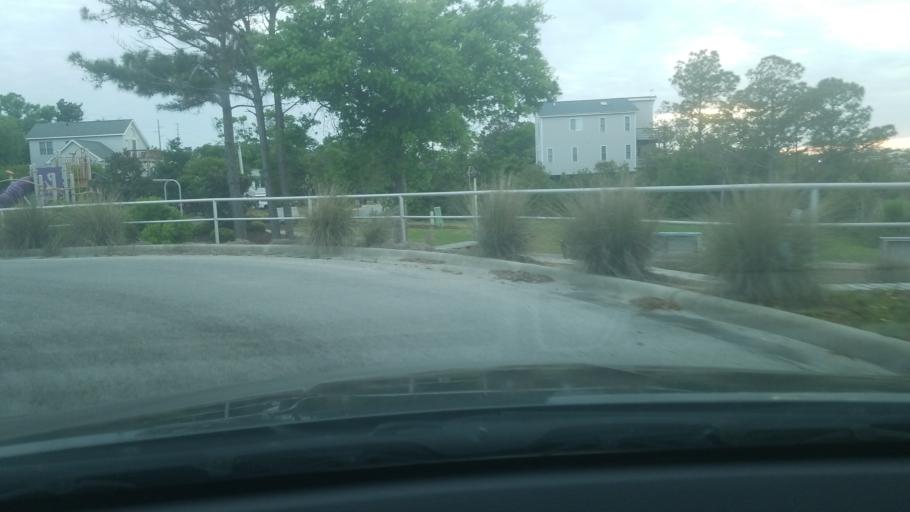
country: US
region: North Carolina
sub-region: Carteret County
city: Emerald Isle
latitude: 34.6706
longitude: -77.0076
